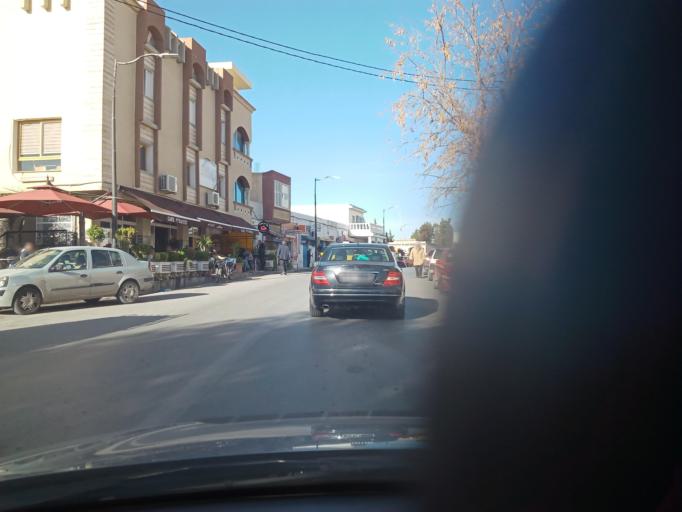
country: TN
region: Kef
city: El Kef
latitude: 36.1779
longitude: 8.7144
